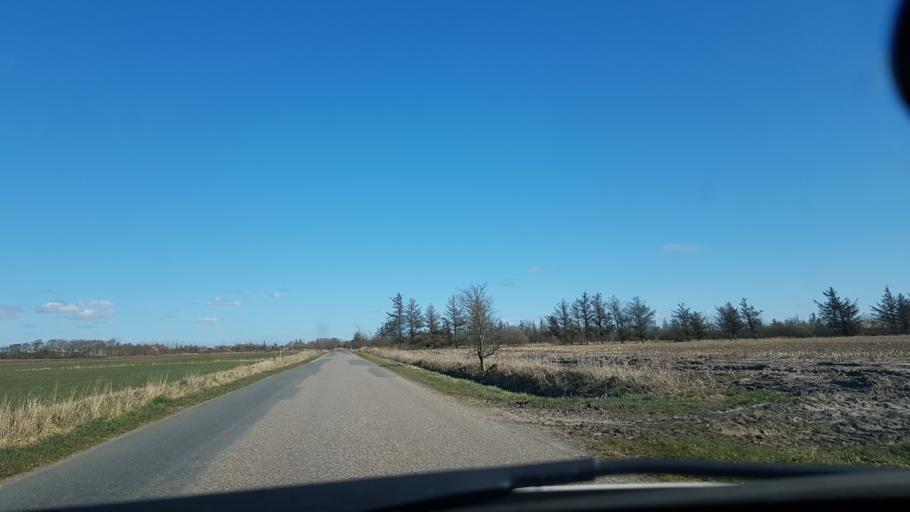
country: DK
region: South Denmark
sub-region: Tonder Kommune
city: Sherrebek
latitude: 55.2293
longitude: 8.7440
